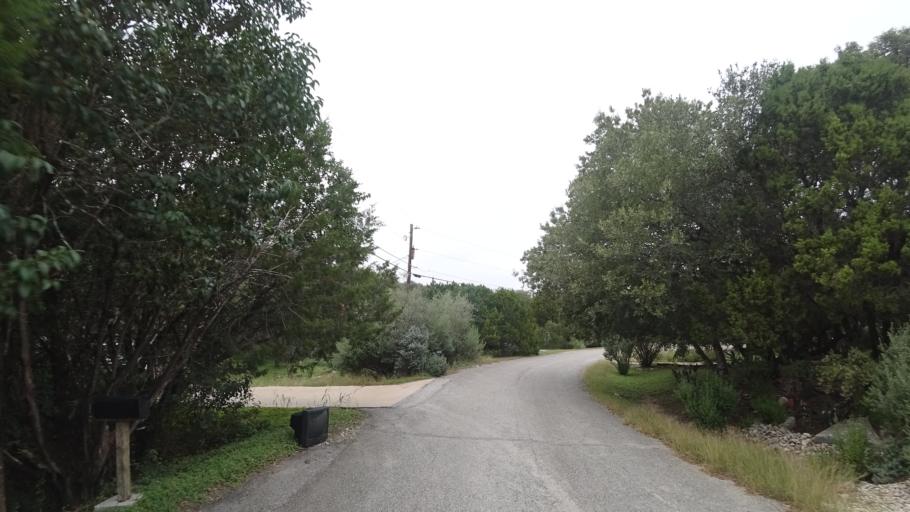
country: US
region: Texas
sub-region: Travis County
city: Hudson Bend
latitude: 30.3736
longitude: -97.9351
